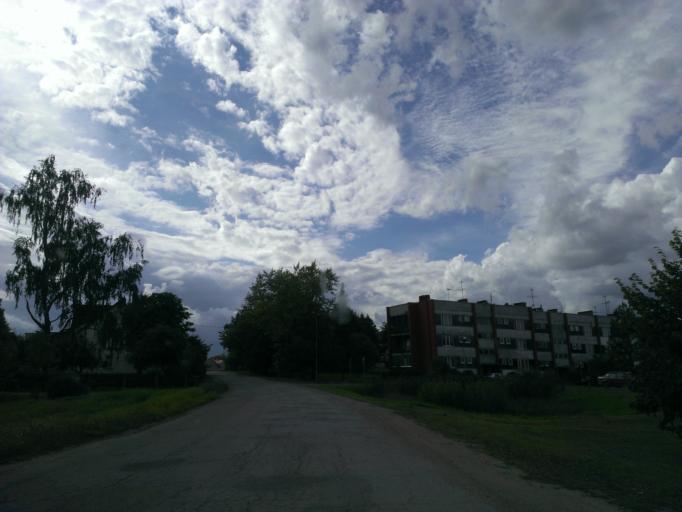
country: LV
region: Skriveri
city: Skriveri
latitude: 56.8461
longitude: 25.1649
